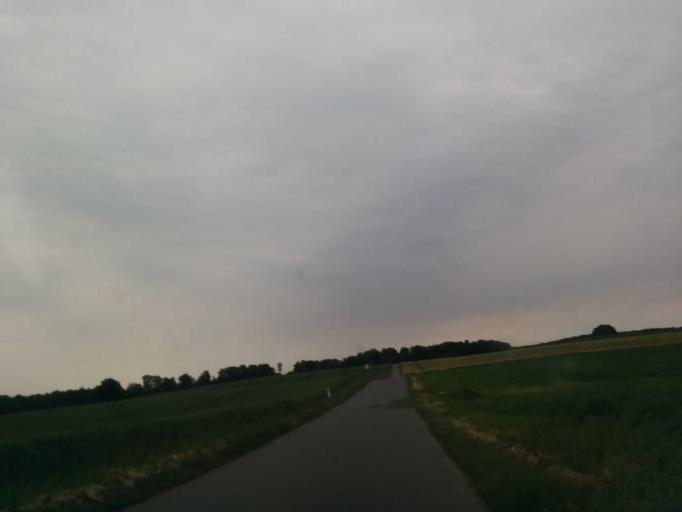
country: DK
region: Central Jutland
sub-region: Arhus Kommune
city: Logten
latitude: 56.2819
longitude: 10.3636
